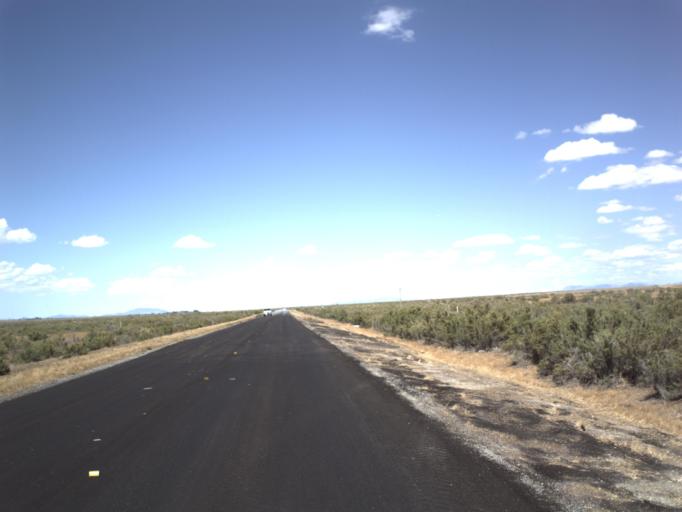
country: US
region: Utah
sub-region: Millard County
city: Delta
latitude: 39.3208
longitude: -112.4820
